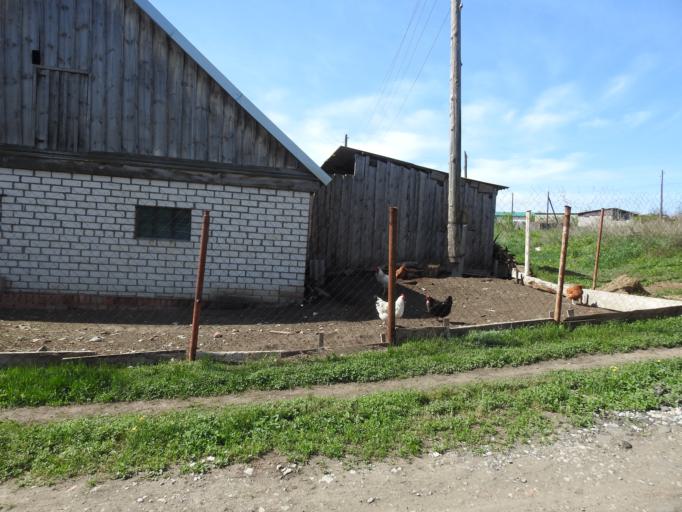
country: RU
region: Saratov
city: Krasnyy Oktyabr'
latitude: 51.6068
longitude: 45.7022
